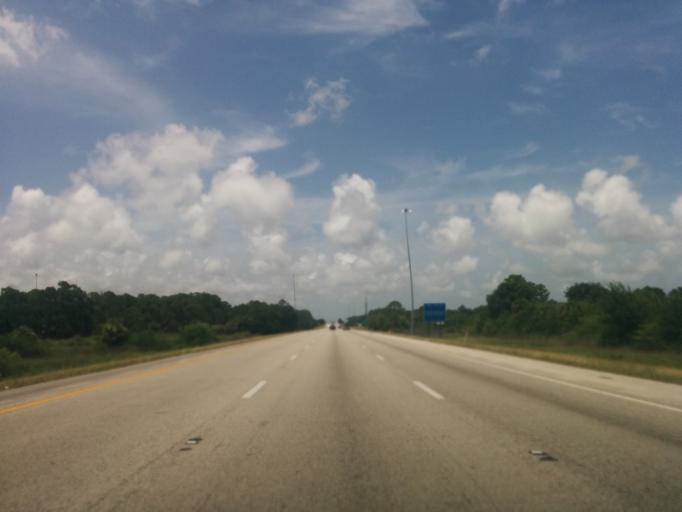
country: US
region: Florida
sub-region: Saint Lucie County
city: Fort Pierce South
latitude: 27.3659
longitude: -80.4125
